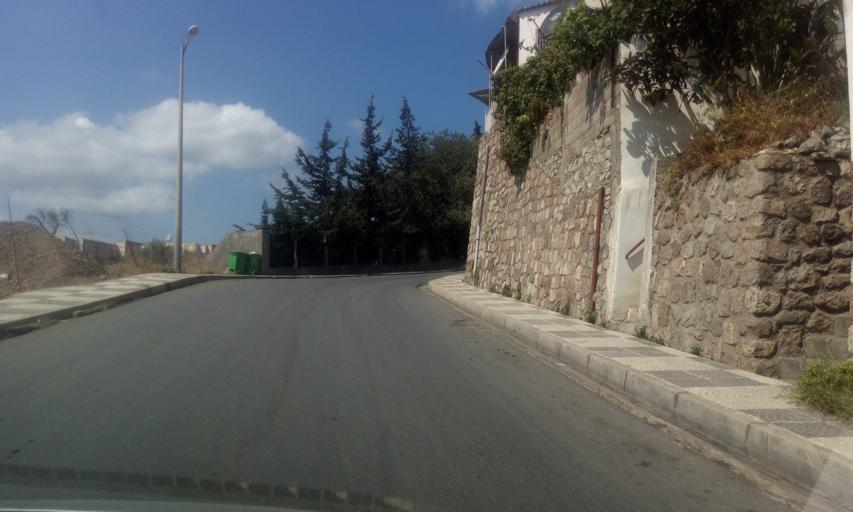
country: DZ
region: Bejaia
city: Bejaia
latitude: 36.7576
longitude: 5.0871
